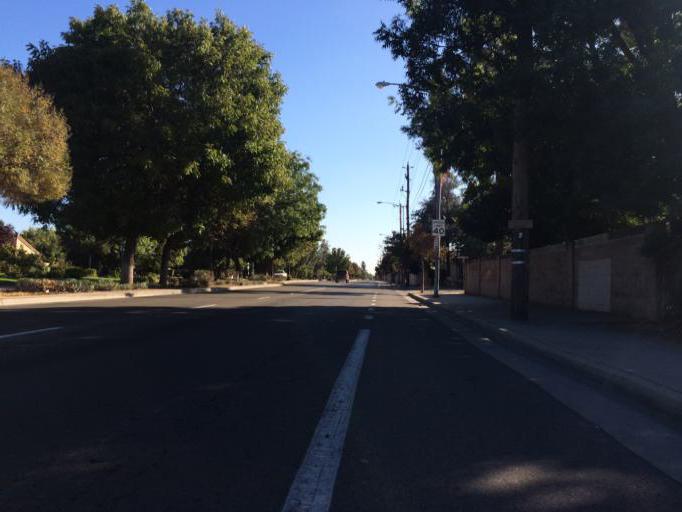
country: US
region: California
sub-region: Fresno County
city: Clovis
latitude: 36.8153
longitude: -119.6822
